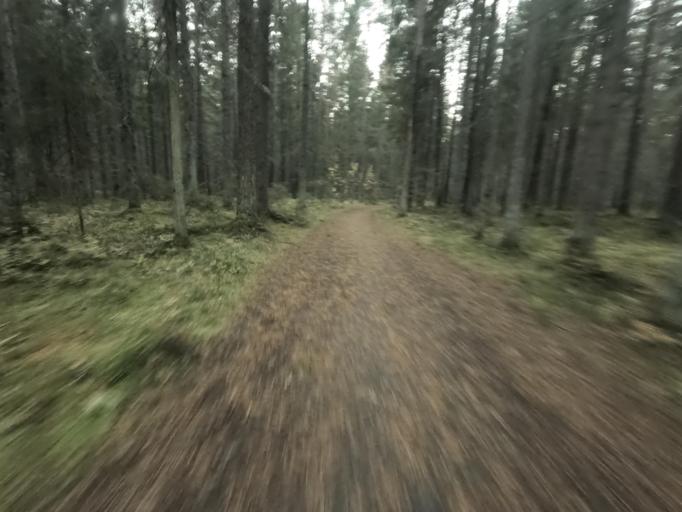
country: RU
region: Leningrad
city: Leninskoye
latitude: 60.1996
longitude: 29.8317
